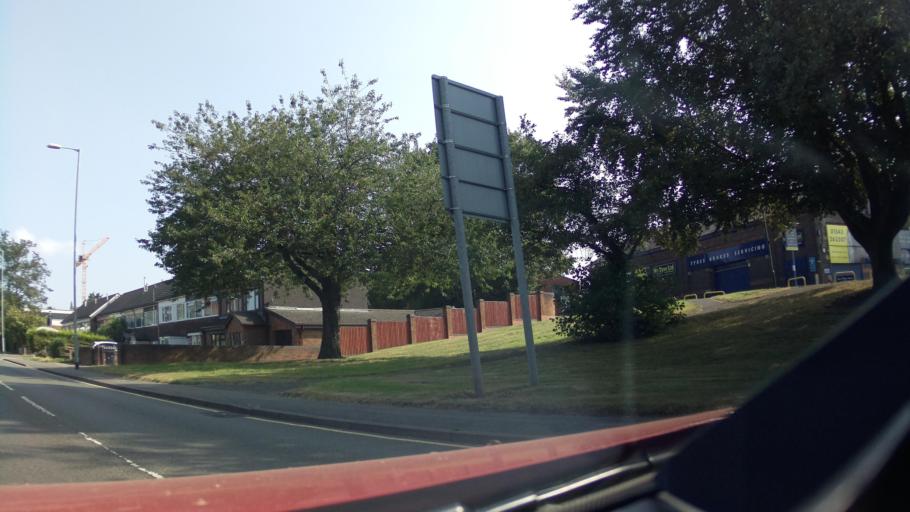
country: GB
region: England
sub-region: Staffordshire
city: Lichfield
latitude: 52.6809
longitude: -1.8255
